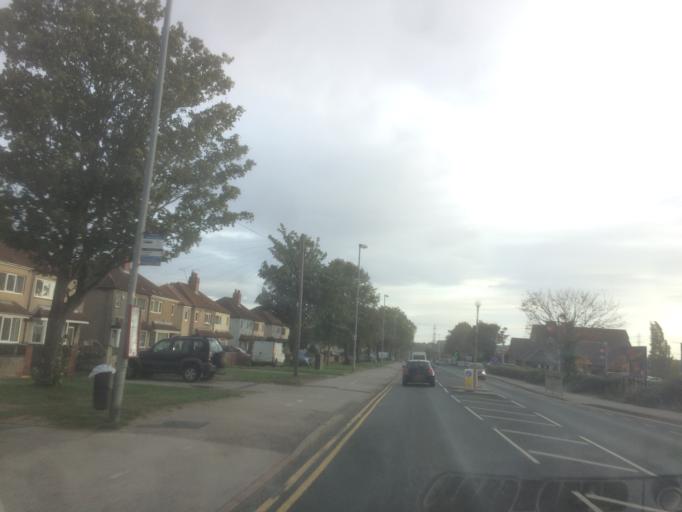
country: GB
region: England
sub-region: City and Borough of Wakefield
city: Castleford
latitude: 53.7140
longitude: -1.3343
